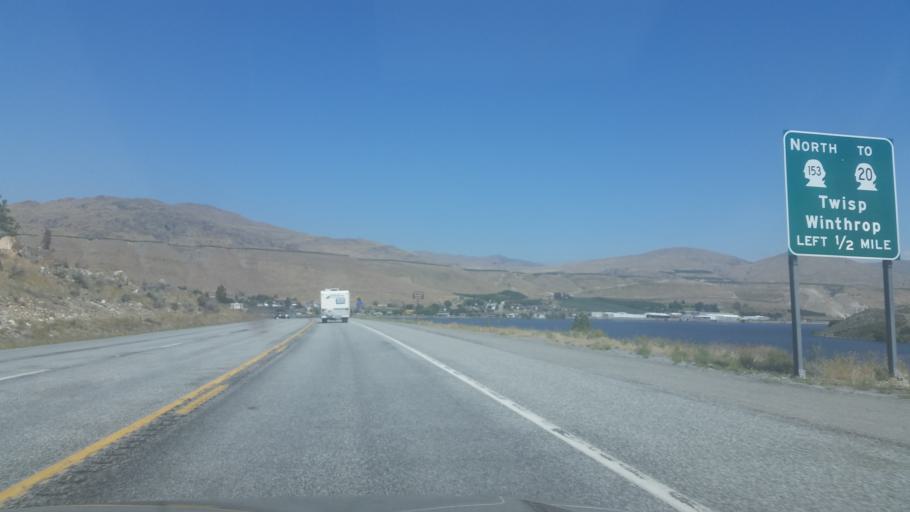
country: US
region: Washington
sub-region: Okanogan County
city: Brewster
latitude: 48.0415
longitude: -119.8965
